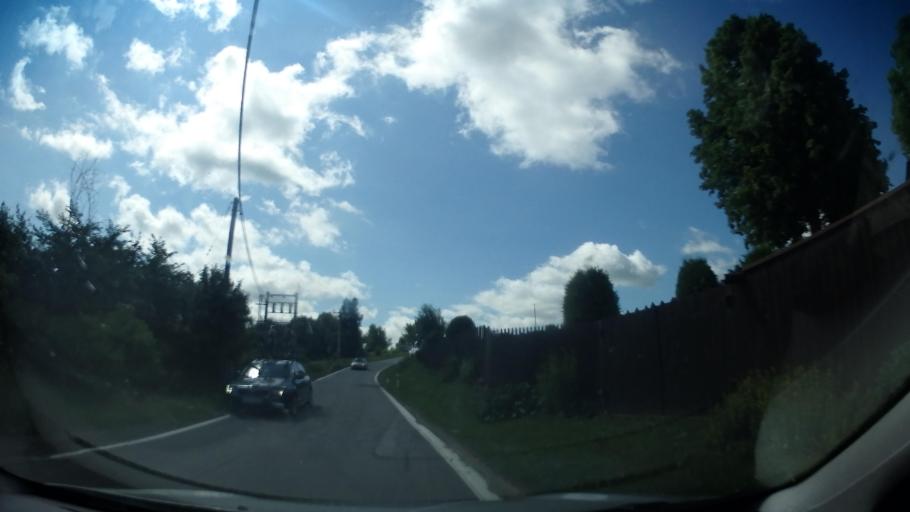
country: CZ
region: Vysocina
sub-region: Okres Zd'ar nad Sazavou
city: Nove Mesto na Morave
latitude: 49.6416
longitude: 16.0965
